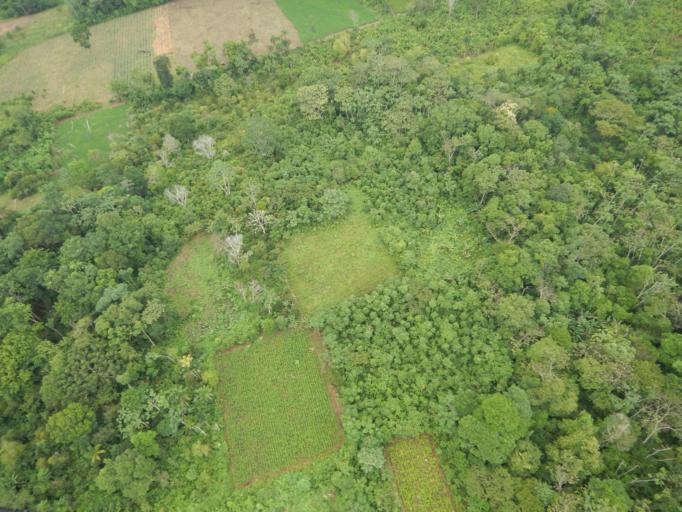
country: BO
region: Cochabamba
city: Chimore
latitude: -17.2319
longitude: -64.6910
